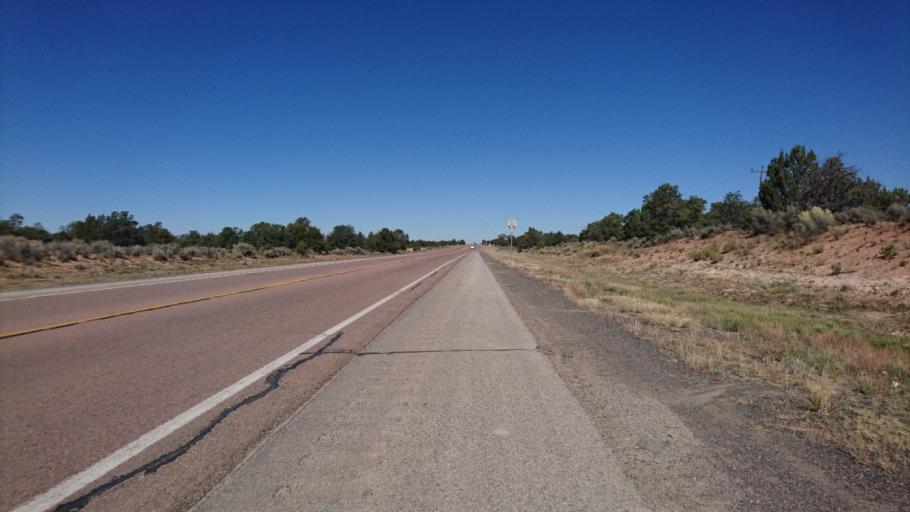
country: US
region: New Mexico
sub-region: McKinley County
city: Gallup
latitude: 35.3592
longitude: -108.7553
